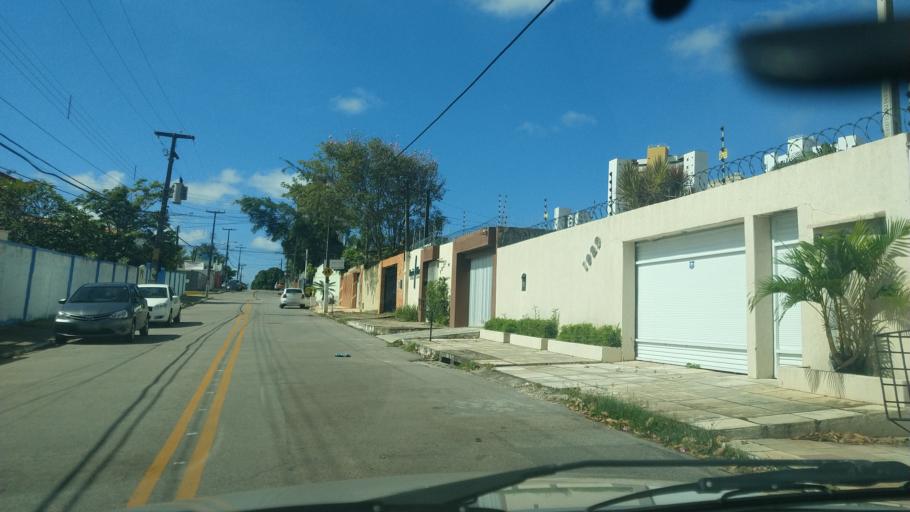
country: BR
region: Rio Grande do Norte
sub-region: Natal
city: Natal
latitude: -5.8600
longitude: -35.2011
